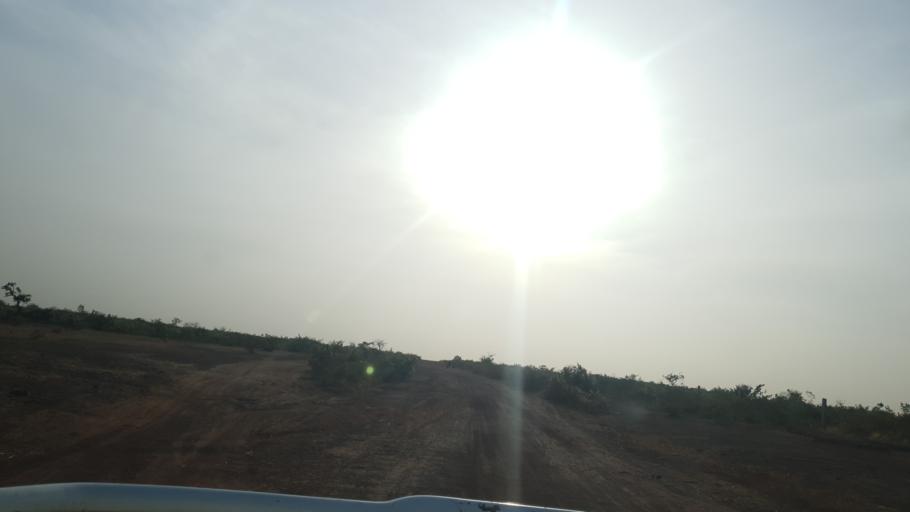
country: ML
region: Koulikoro
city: Dioila
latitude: 12.7682
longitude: -6.9236
